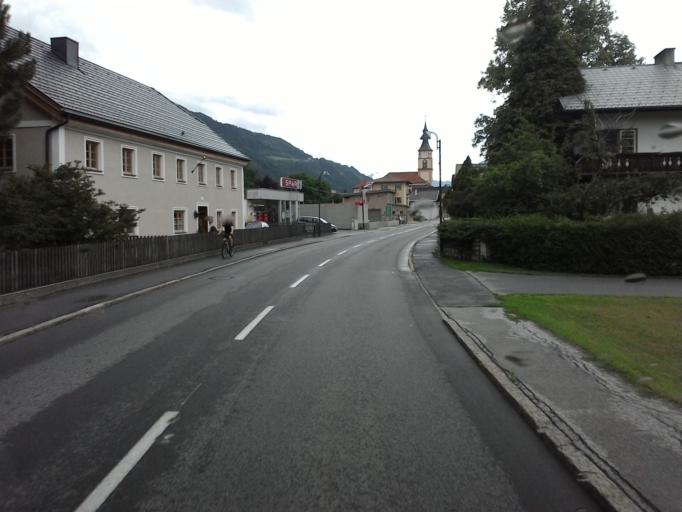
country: AT
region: Tyrol
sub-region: Politischer Bezirk Imst
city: Silz
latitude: 47.2668
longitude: 10.9316
